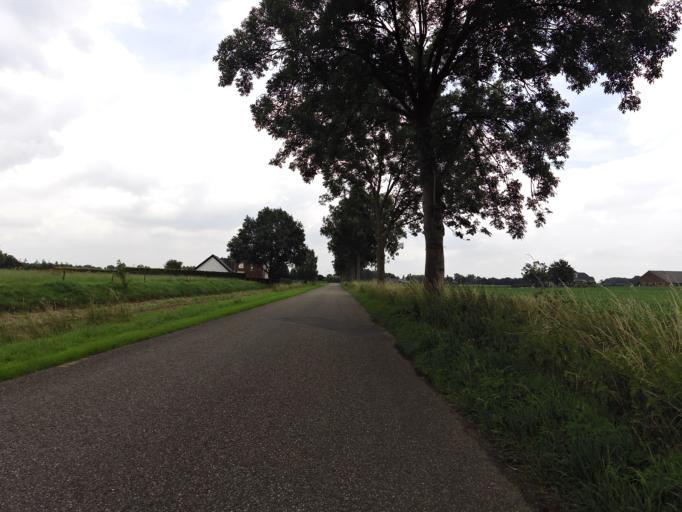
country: NL
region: Gelderland
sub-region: Gemeente Zevenaar
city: Zevenaar
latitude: 51.9211
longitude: 6.1451
